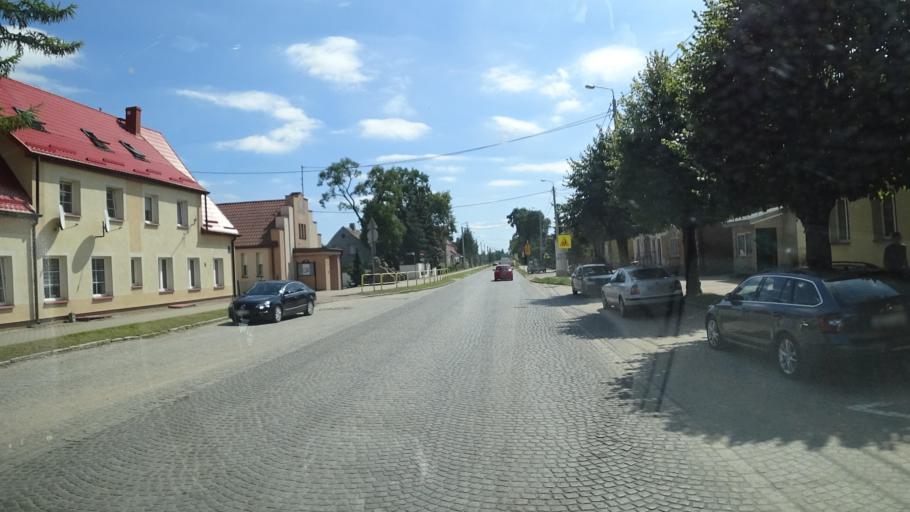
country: PL
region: Warmian-Masurian Voivodeship
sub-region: Powiat elcki
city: Prostki
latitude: 53.6962
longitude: 22.4371
